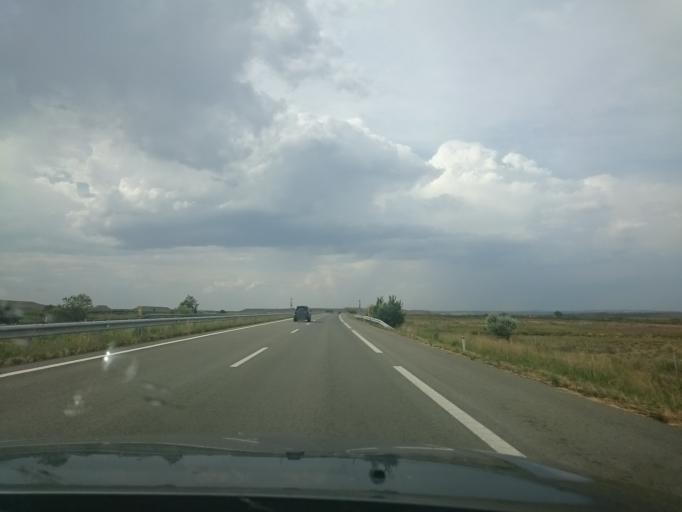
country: ES
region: La Rioja
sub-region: Provincia de La Rioja
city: Rincon de Soto
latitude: 42.1787
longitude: -1.8372
